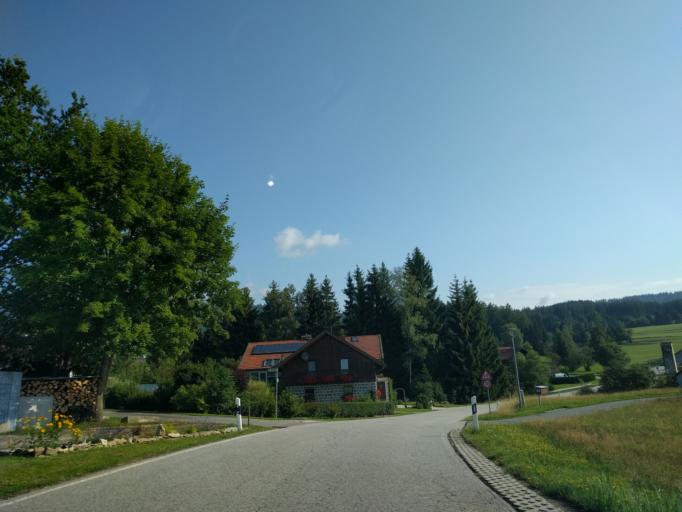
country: DE
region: Bavaria
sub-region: Lower Bavaria
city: Hohenau
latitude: 48.8638
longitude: 13.5379
